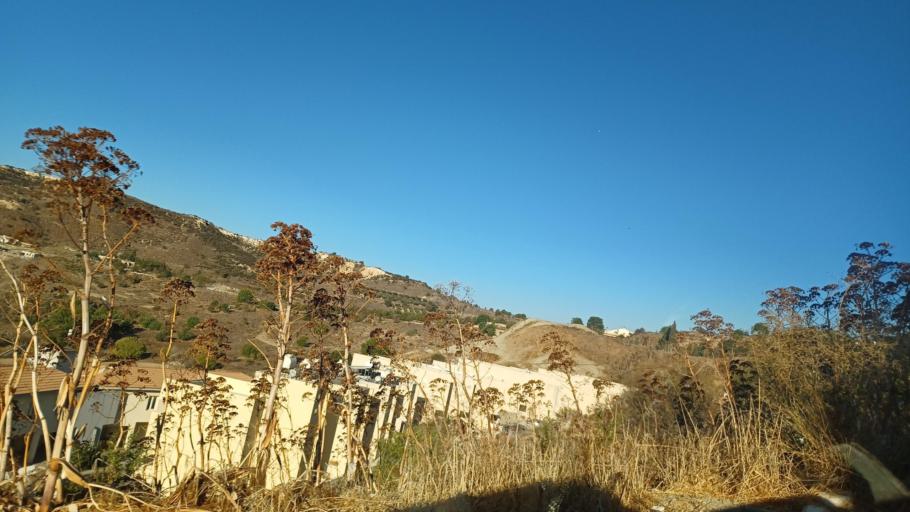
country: CY
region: Pafos
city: Mesogi
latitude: 34.7901
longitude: 32.4864
